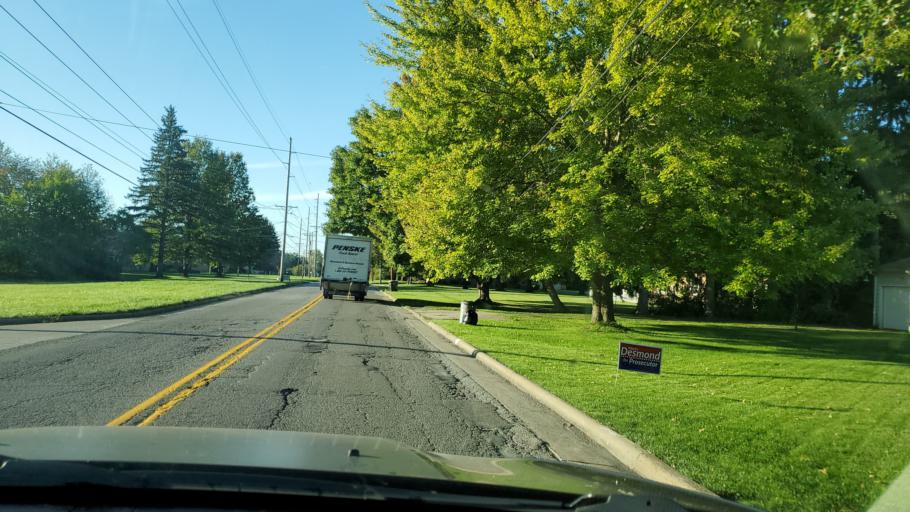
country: US
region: Ohio
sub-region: Mahoning County
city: Struthers
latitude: 41.0421
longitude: -80.6214
